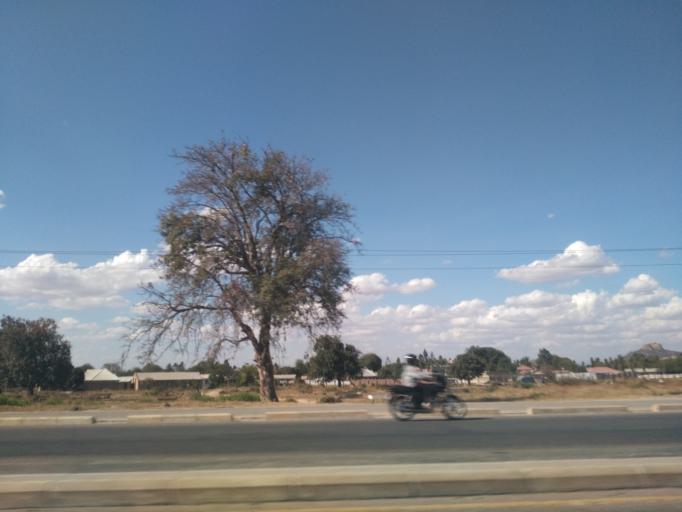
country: TZ
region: Dodoma
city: Dodoma
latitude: -6.1713
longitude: 35.7307
